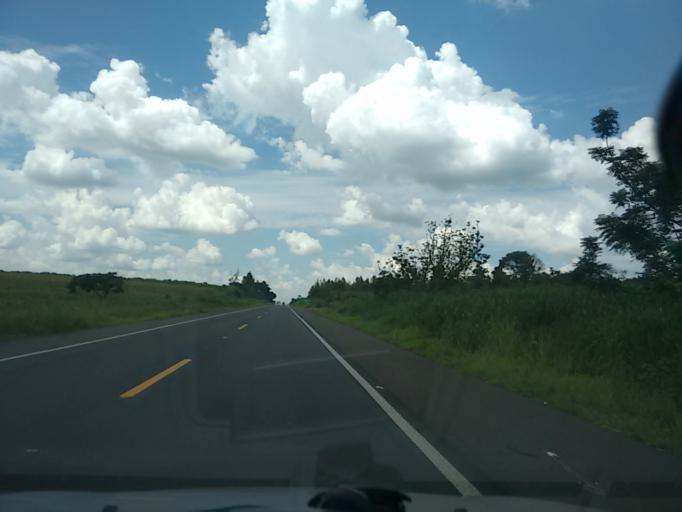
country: BR
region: Sao Paulo
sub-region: Osvaldo Cruz
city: Osvaldo Cruz
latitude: -21.8553
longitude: -50.8410
